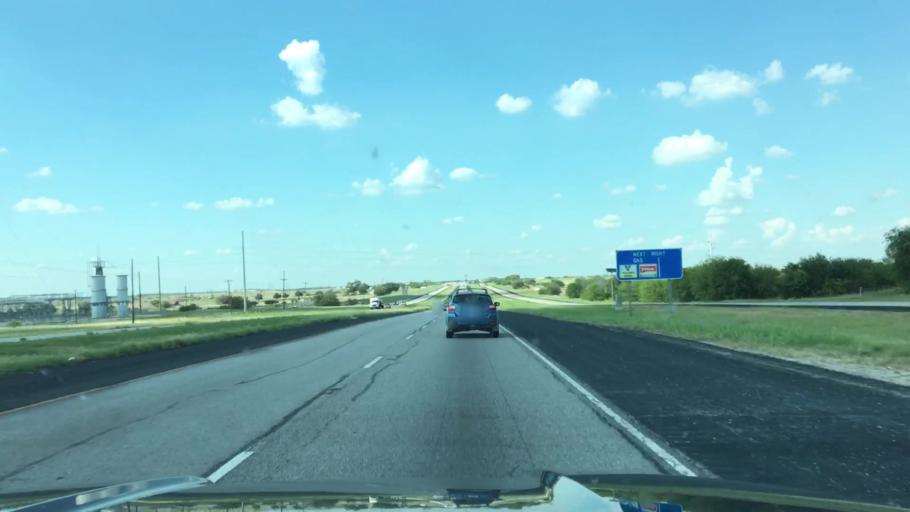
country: US
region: Texas
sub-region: Wise County
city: Rhome
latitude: 33.0740
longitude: -97.4731
